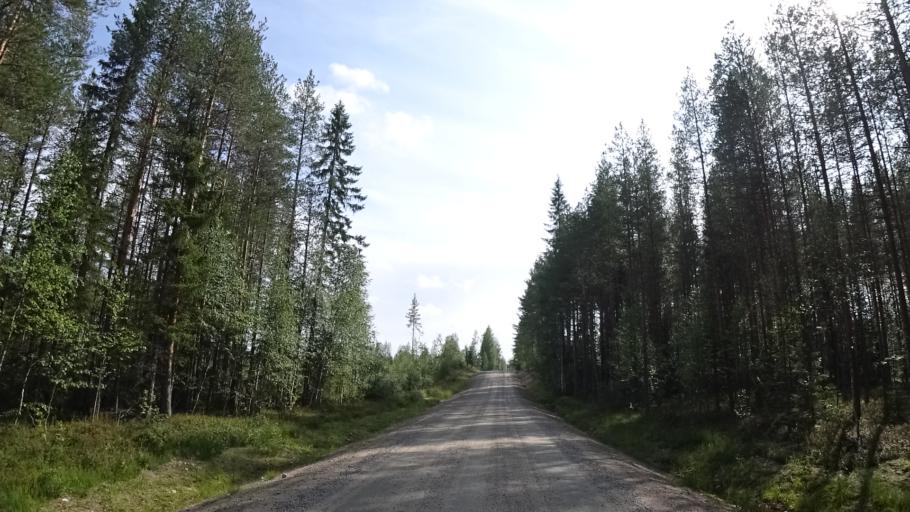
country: FI
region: North Karelia
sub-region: Pielisen Karjala
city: Lieksa
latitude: 63.5896
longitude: 30.1352
